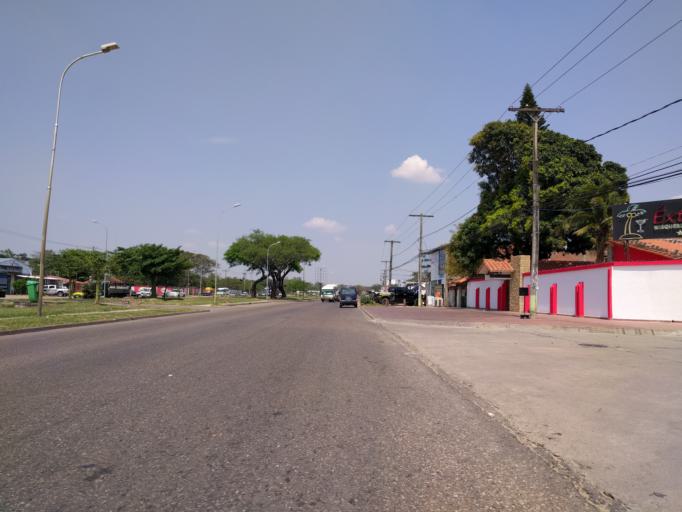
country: BO
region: Santa Cruz
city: Santa Cruz de la Sierra
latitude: -17.8081
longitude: -63.1567
